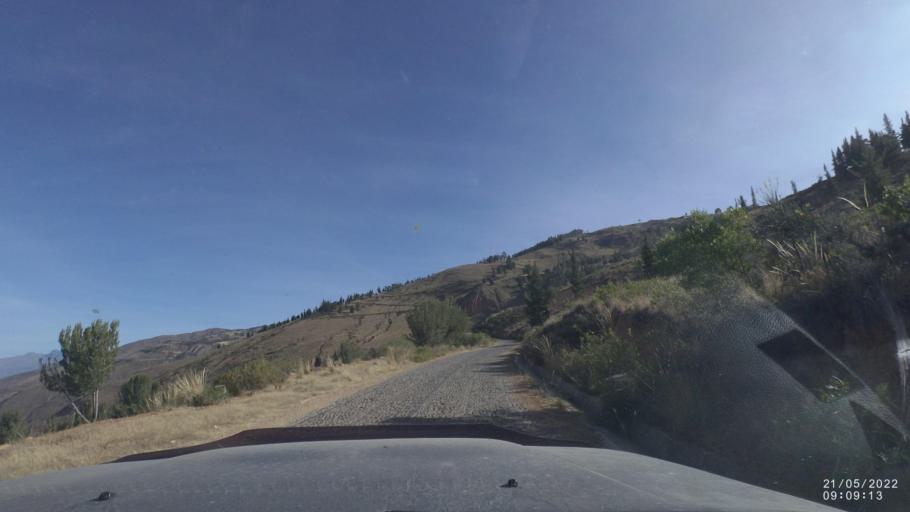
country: BO
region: Cochabamba
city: Cochabamba
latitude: -17.3747
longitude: -66.0240
